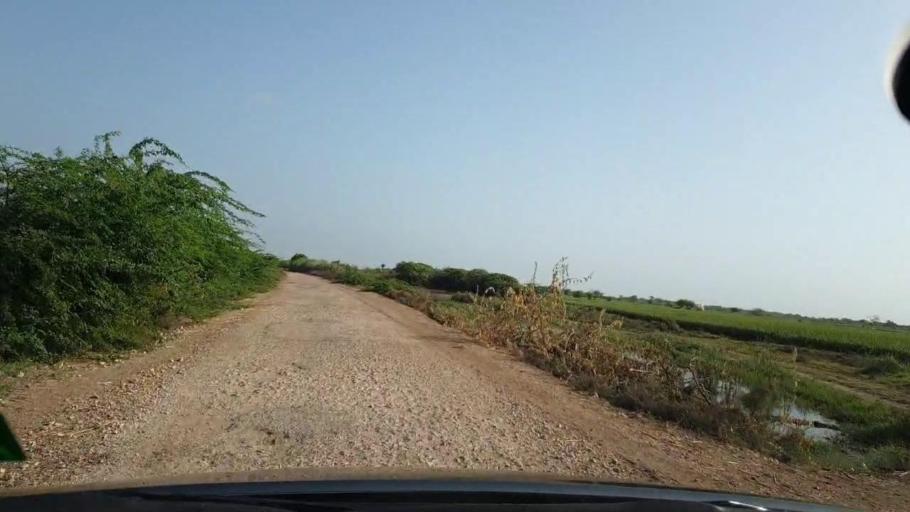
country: PK
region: Sindh
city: Tando Bago
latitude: 24.6546
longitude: 69.0412
